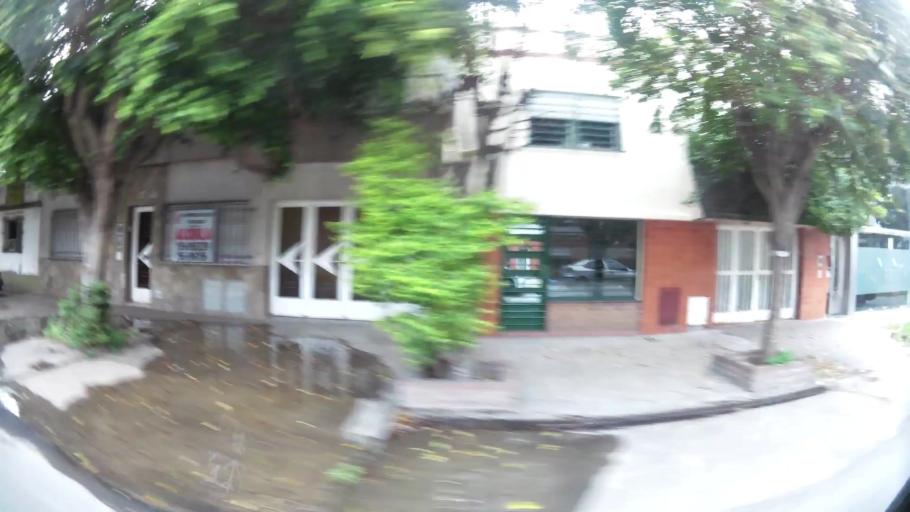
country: AR
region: Santa Fe
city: Gobernador Galvez
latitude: -32.9927
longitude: -60.6537
